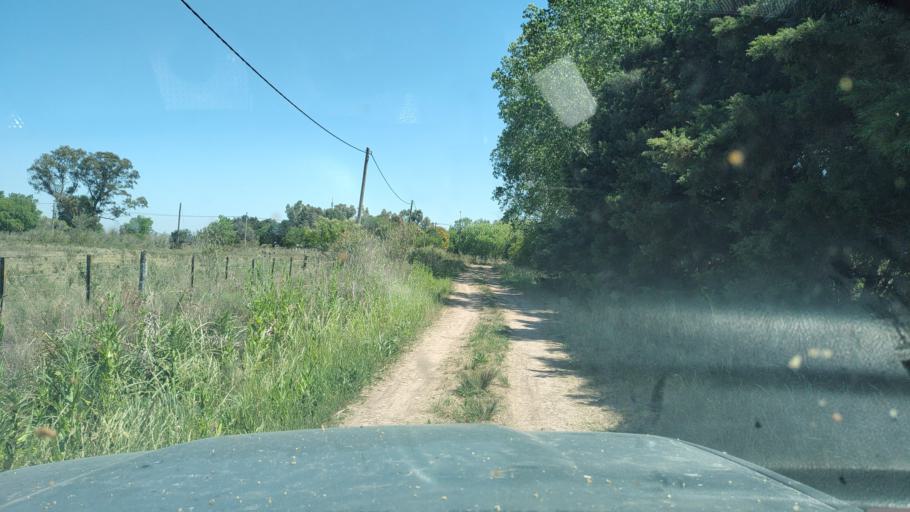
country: AR
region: Buenos Aires
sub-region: Partido de Lujan
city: Lujan
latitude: -34.6002
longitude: -59.1400
